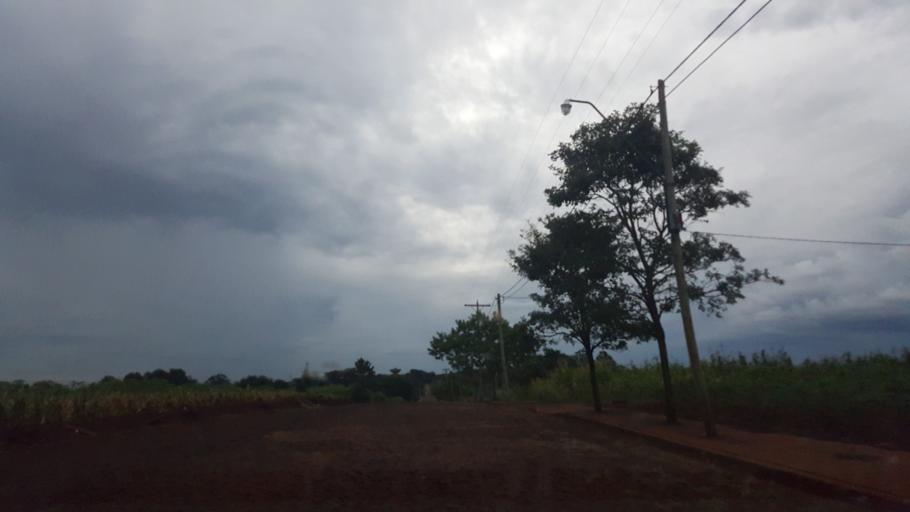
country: AR
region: Misiones
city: Capiovi
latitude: -26.9349
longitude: -55.0482
